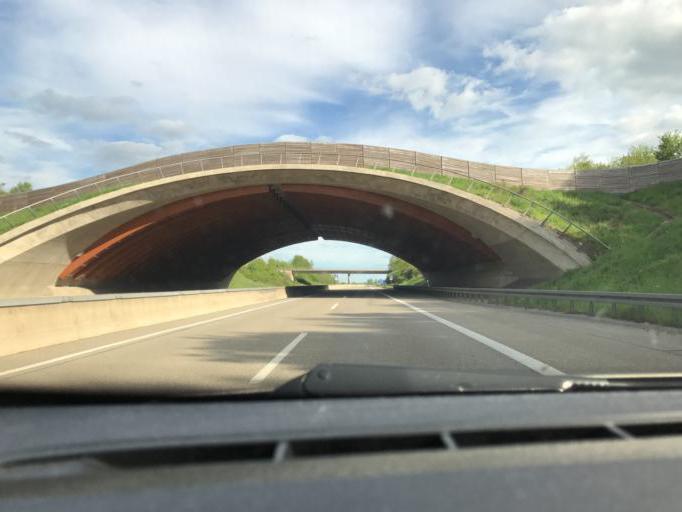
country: DE
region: North Rhine-Westphalia
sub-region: Regierungsbezirk Koln
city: Nettersheim
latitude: 50.4803
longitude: 6.6844
